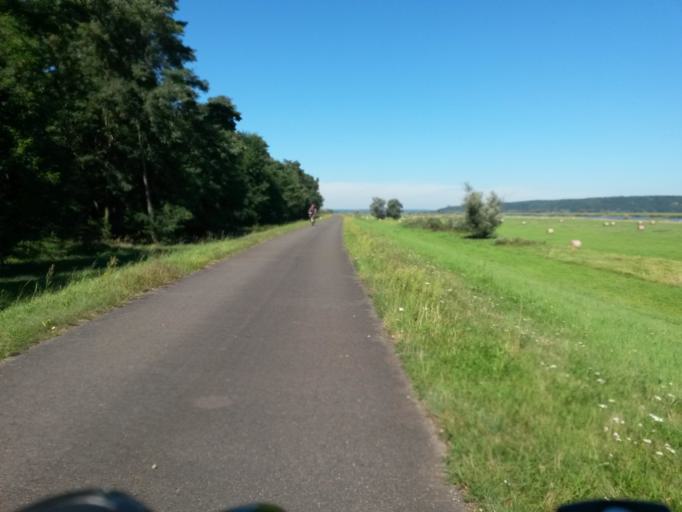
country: PL
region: West Pomeranian Voivodeship
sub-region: Powiat gryfinski
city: Cedynia
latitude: 52.9021
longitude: 14.1486
